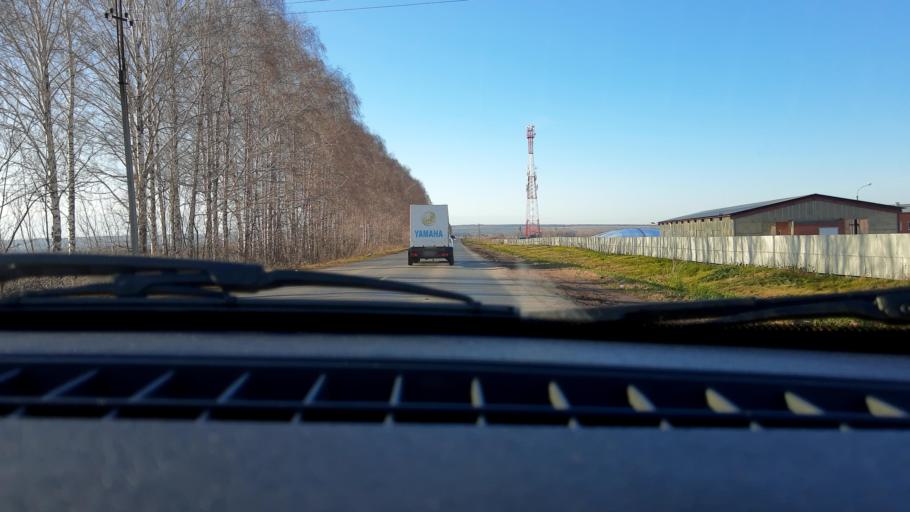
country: RU
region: Bashkortostan
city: Ufa
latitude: 54.8244
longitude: 55.9850
